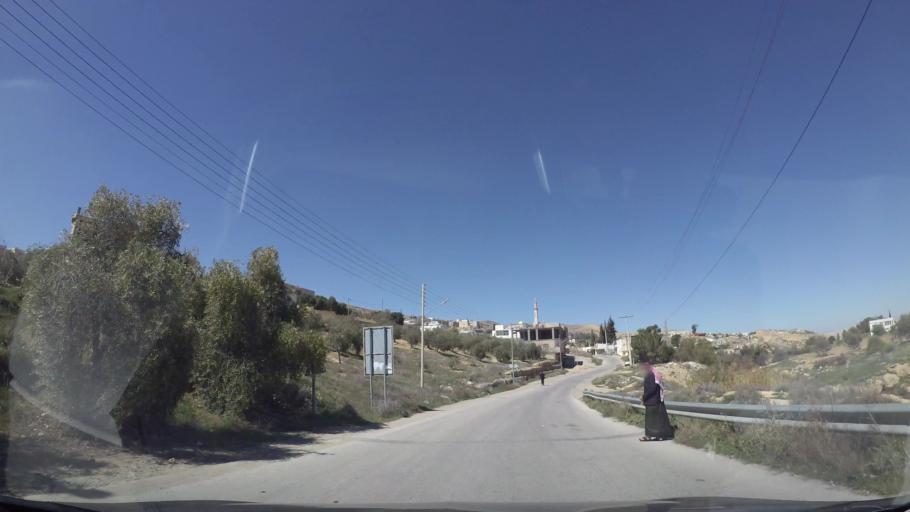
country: JO
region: Tafielah
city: At Tafilah
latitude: 30.8181
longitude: 35.5860
